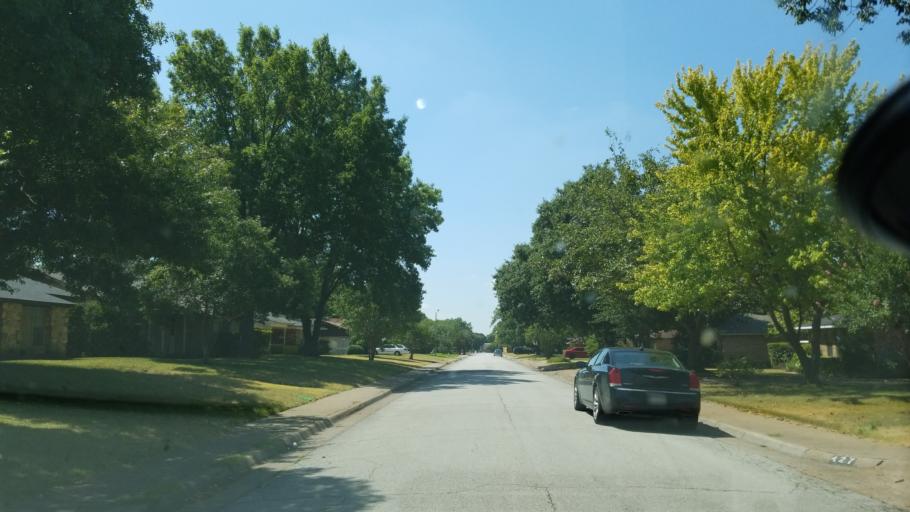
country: US
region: Texas
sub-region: Dallas County
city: Duncanville
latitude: 32.6562
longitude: -96.8952
